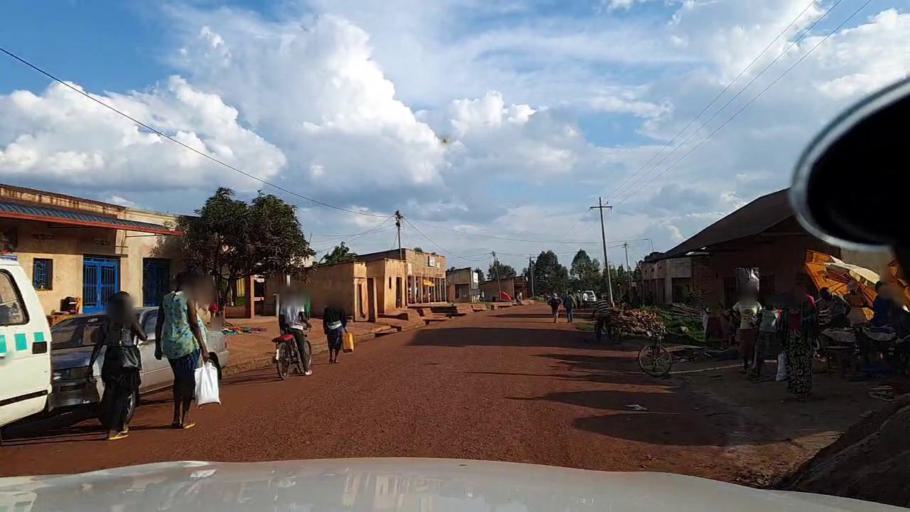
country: RW
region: Kigali
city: Kigali
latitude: -1.9067
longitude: 29.9800
